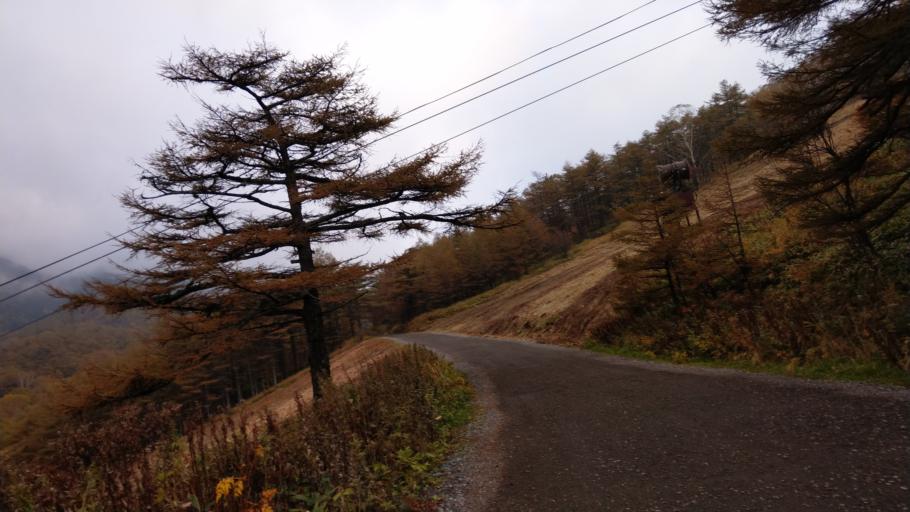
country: JP
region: Nagano
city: Komoro
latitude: 36.4068
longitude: 138.4655
